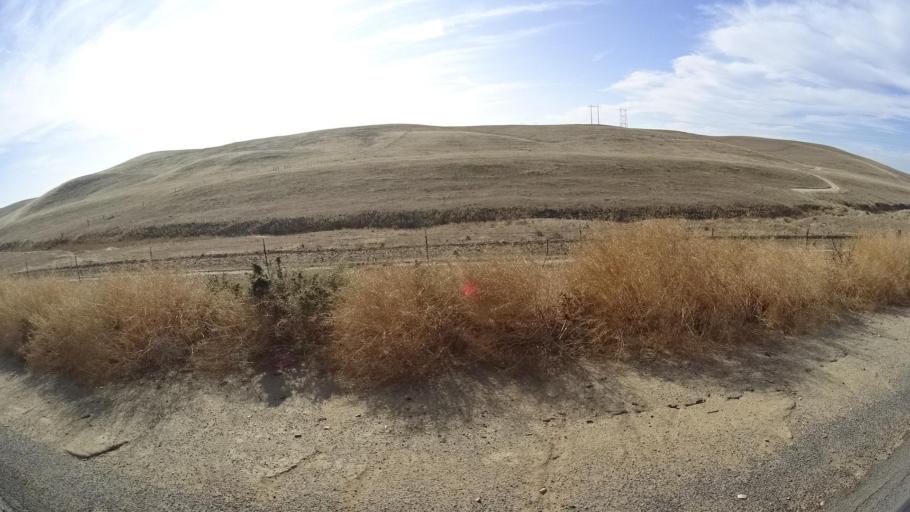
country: US
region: California
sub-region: Tulare County
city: Richgrove
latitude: 35.6202
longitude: -119.0380
